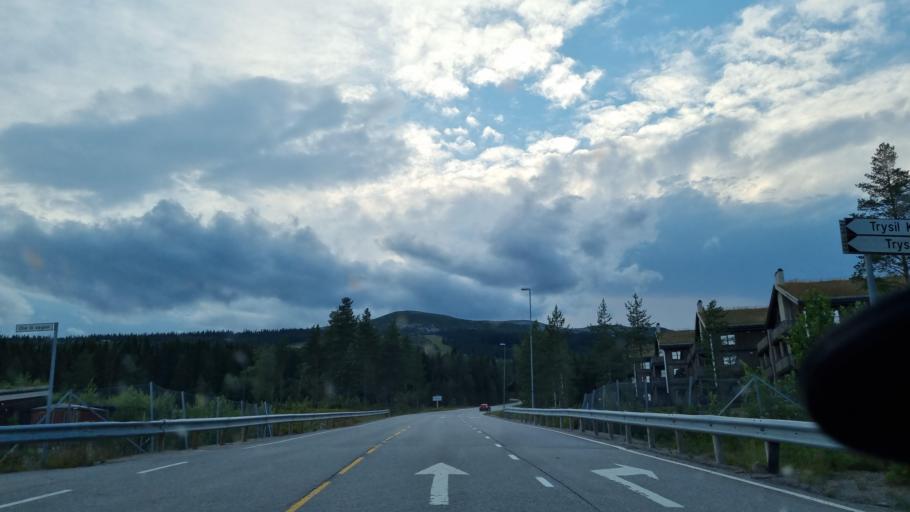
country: NO
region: Hedmark
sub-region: Trysil
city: Innbygda
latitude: 61.3044
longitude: 12.2455
